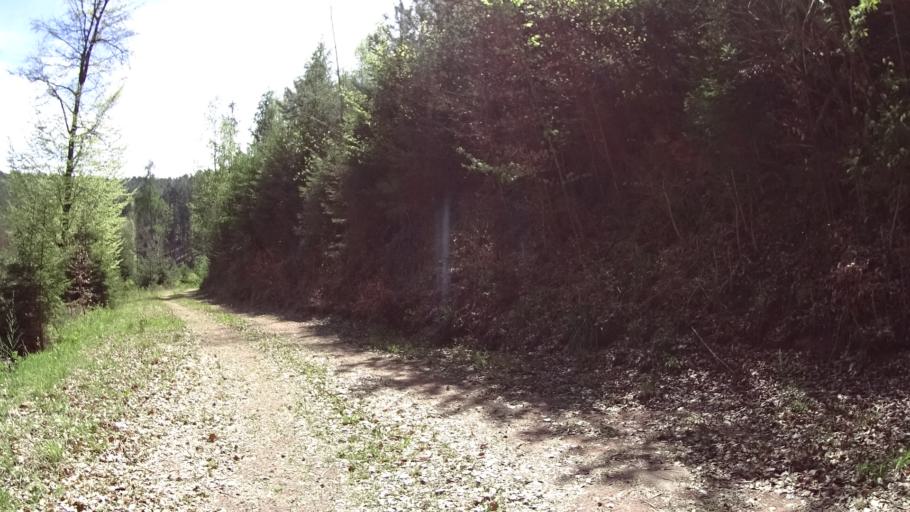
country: DE
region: Rheinland-Pfalz
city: Ramberg
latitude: 49.2962
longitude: 7.9948
